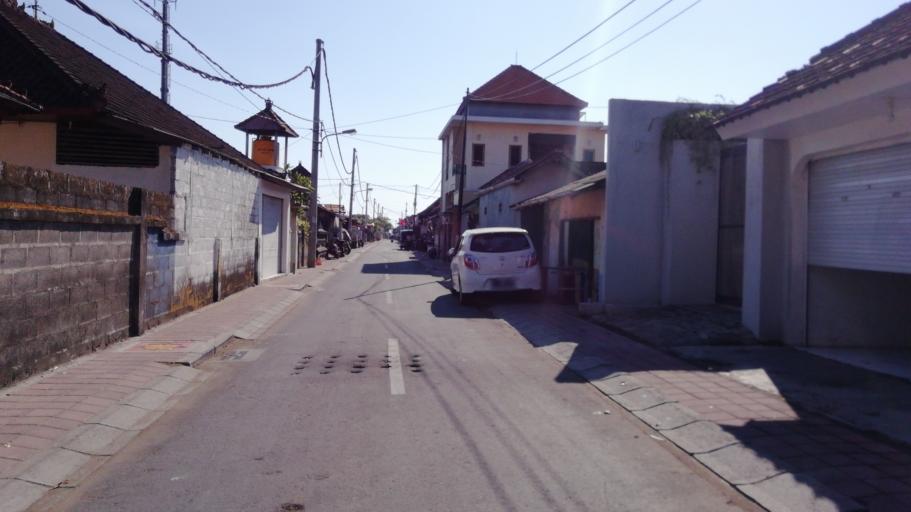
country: ID
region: Bali
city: Bualu
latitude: -8.7557
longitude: 115.2195
